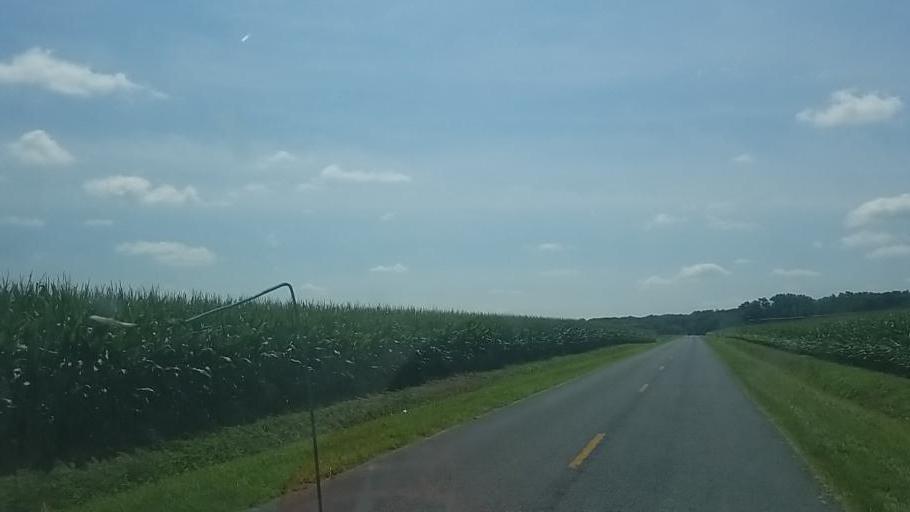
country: US
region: Maryland
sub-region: Caroline County
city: Ridgely
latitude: 38.8995
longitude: -75.9331
